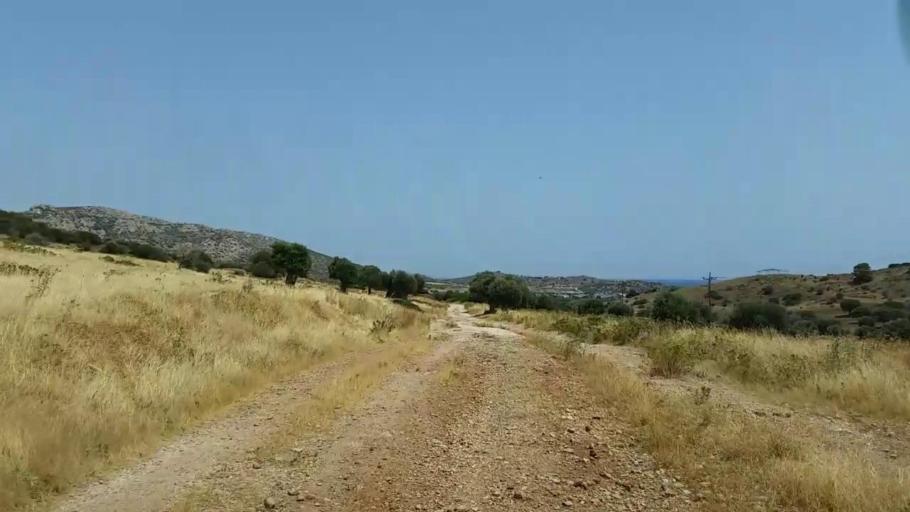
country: GR
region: Attica
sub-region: Nomarchia Anatolikis Attikis
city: Palaia Fokaia
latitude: 37.6768
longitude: 23.9574
